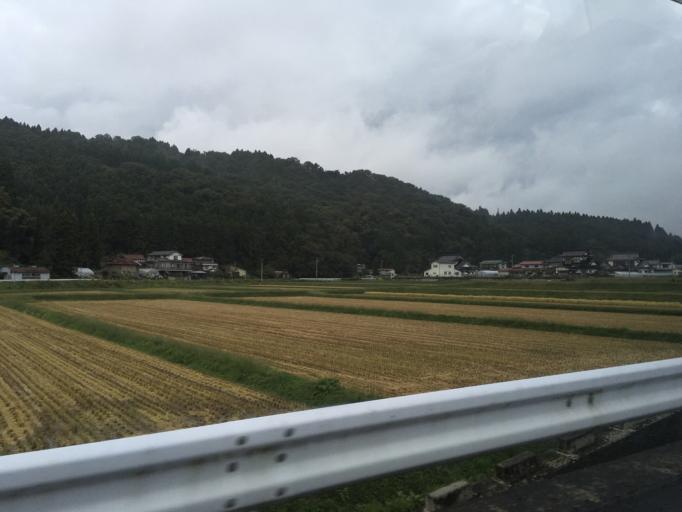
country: JP
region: Iwate
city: Ichinoseki
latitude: 38.8422
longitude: 141.2594
